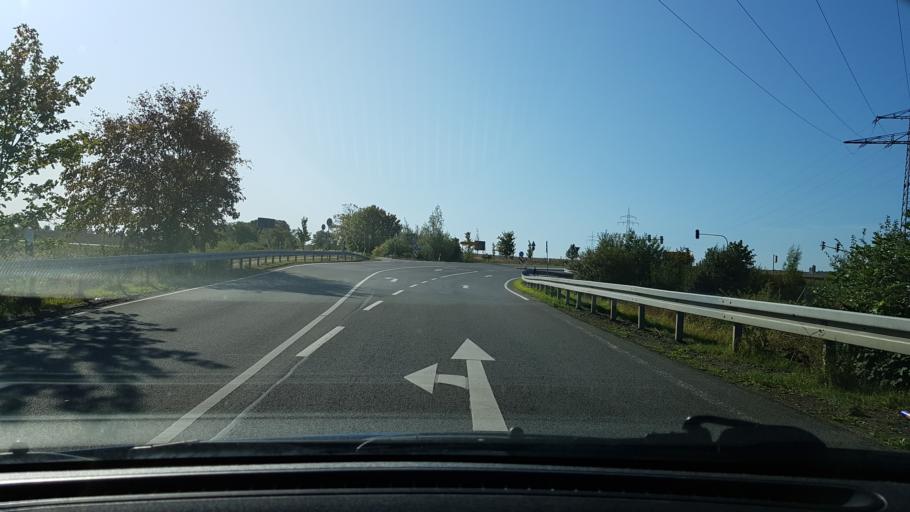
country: DE
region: Lower Saxony
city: Bad Munder am Deister
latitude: 52.2236
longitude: 9.4354
